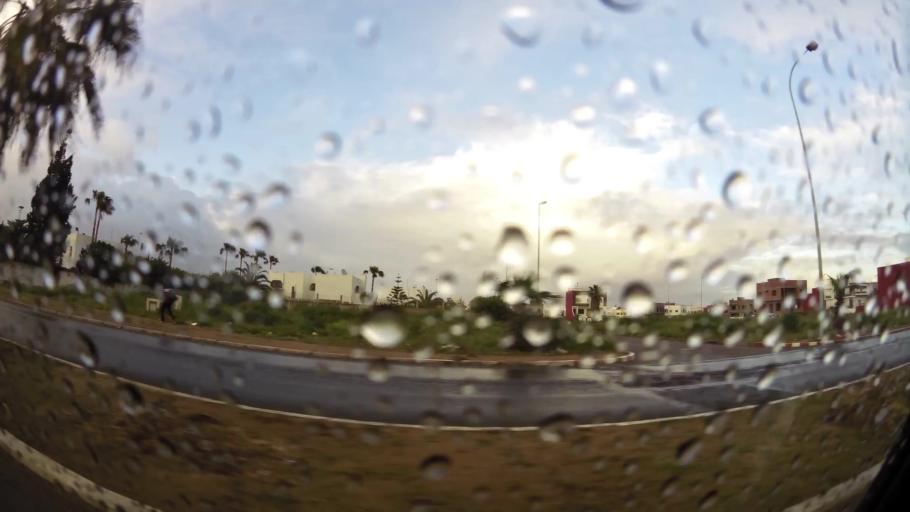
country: MA
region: Doukkala-Abda
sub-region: El-Jadida
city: El Jadida
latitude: 33.2390
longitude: -8.5076
